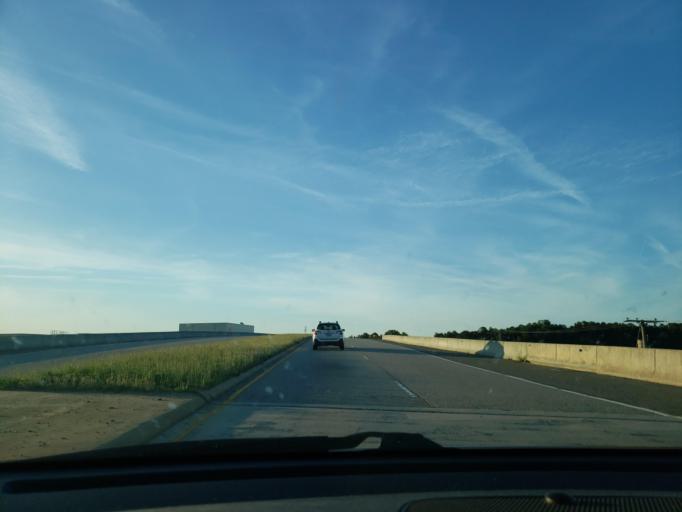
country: US
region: Virginia
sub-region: Henrico County
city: Fort Lee
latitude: 37.4941
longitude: -77.3412
